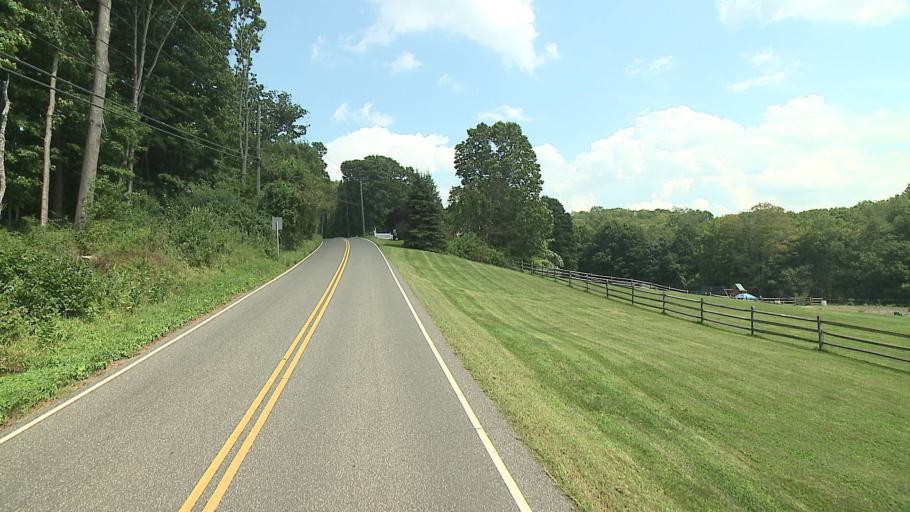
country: US
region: Connecticut
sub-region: Litchfield County
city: New Preston
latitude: 41.6493
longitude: -73.2991
